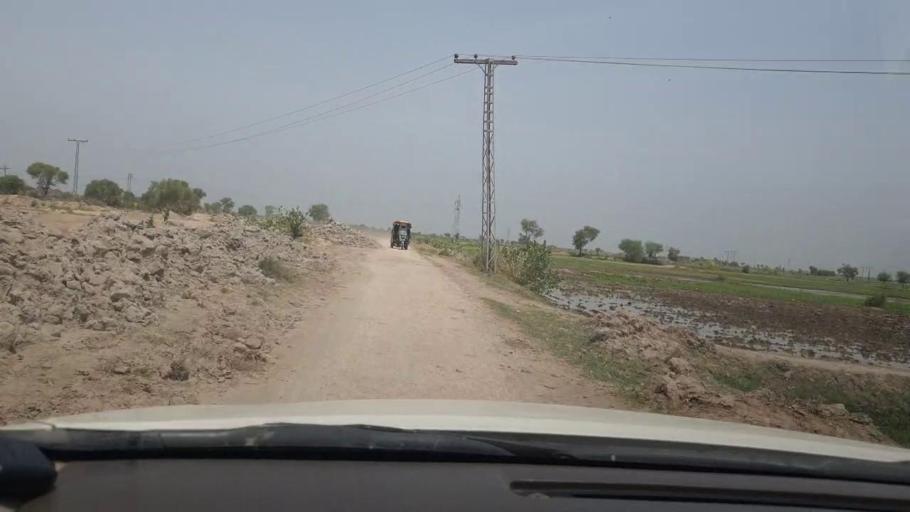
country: PK
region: Sindh
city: Garhi Yasin
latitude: 27.9457
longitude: 68.5287
